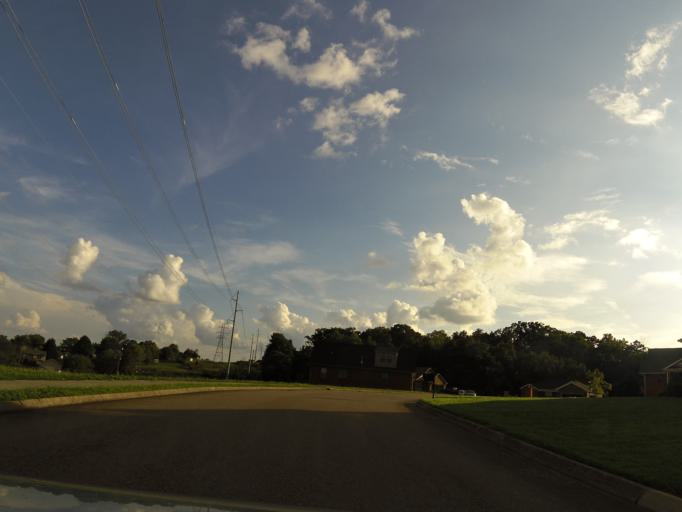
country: US
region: Tennessee
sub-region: Knox County
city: Knoxville
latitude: 35.9992
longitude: -84.0155
